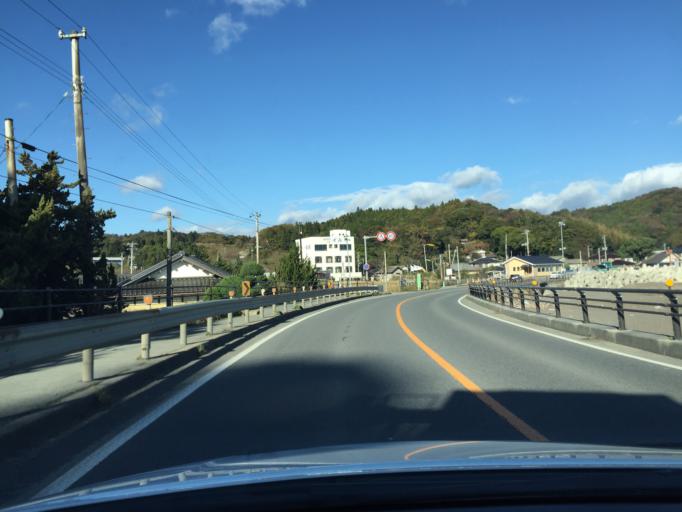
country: JP
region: Fukushima
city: Iwaki
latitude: 37.1191
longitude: 140.9982
